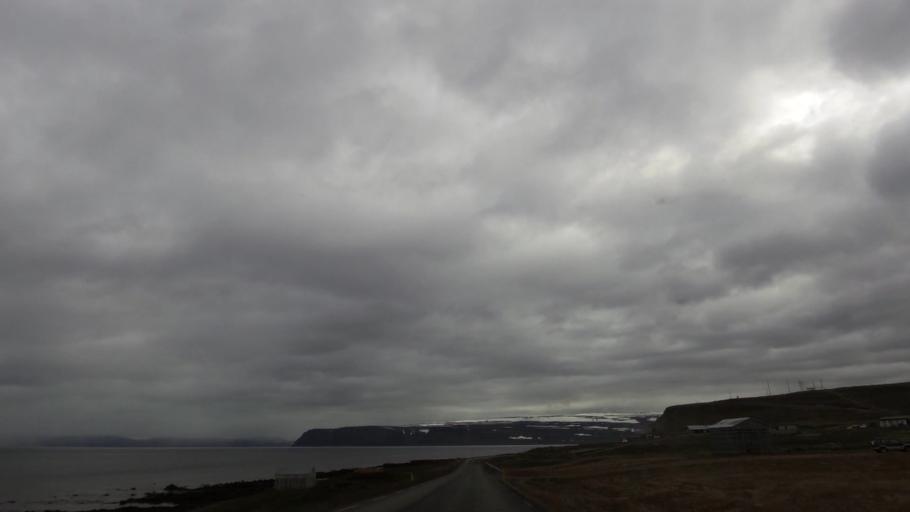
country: IS
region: Westfjords
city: Isafjoerdur
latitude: 66.0945
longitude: -23.0539
